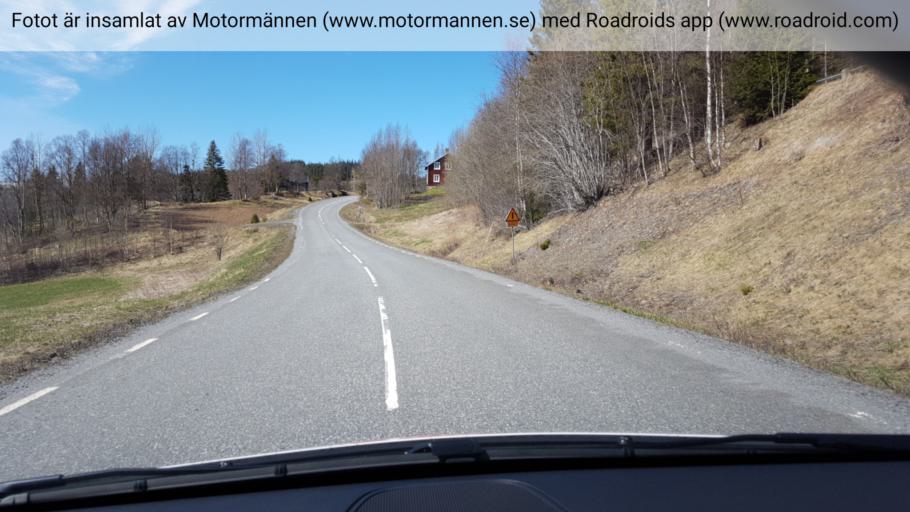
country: SE
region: Jaemtland
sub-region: Are Kommun
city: Are
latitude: 63.5254
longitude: 13.1091
